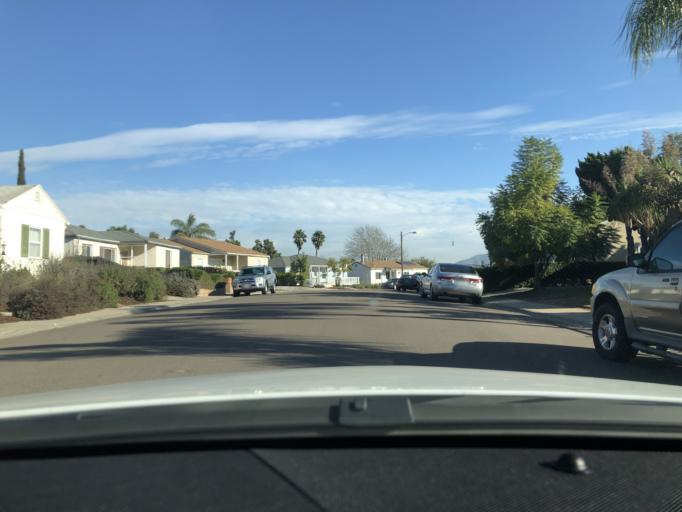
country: US
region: California
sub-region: San Diego County
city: Lemon Grove
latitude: 32.7564
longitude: -117.0677
